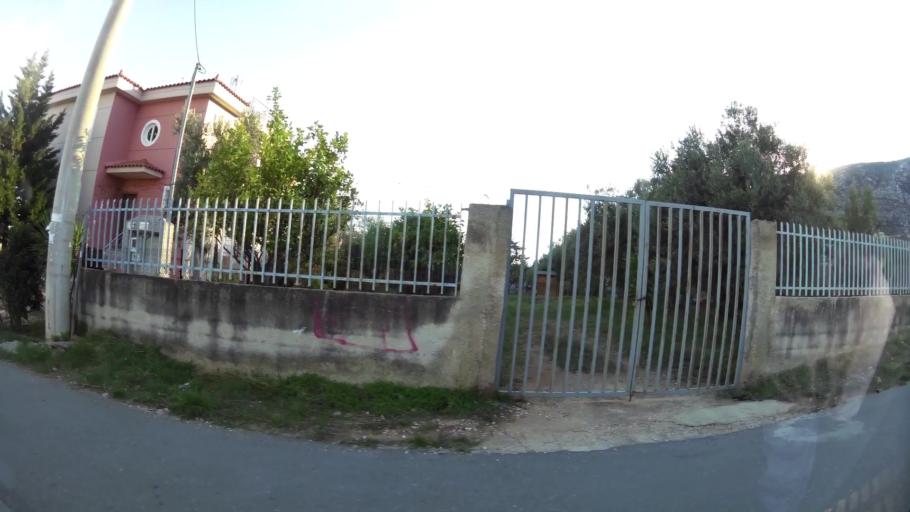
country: GR
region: Attica
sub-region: Nomarchia Anatolikis Attikis
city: Paiania
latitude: 37.9669
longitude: 23.8450
